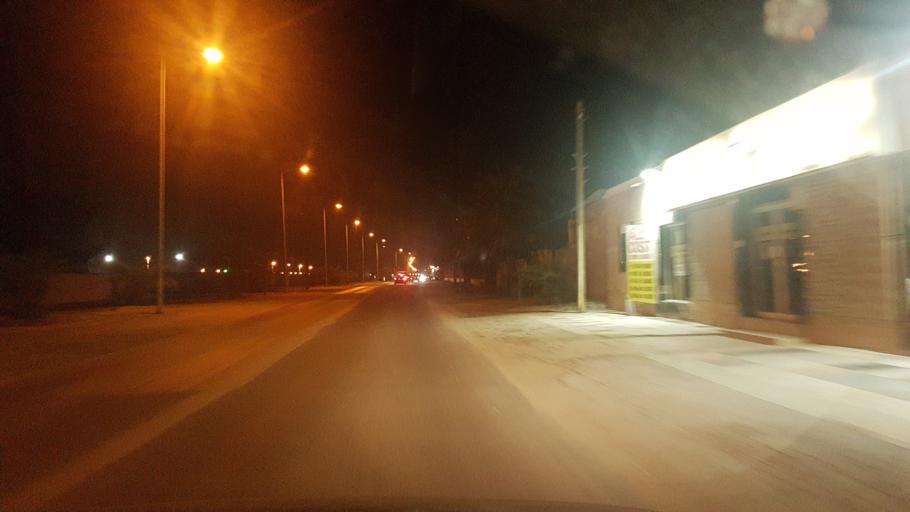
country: BH
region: Muharraq
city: Al Hadd
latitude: 26.2751
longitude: 50.6411
